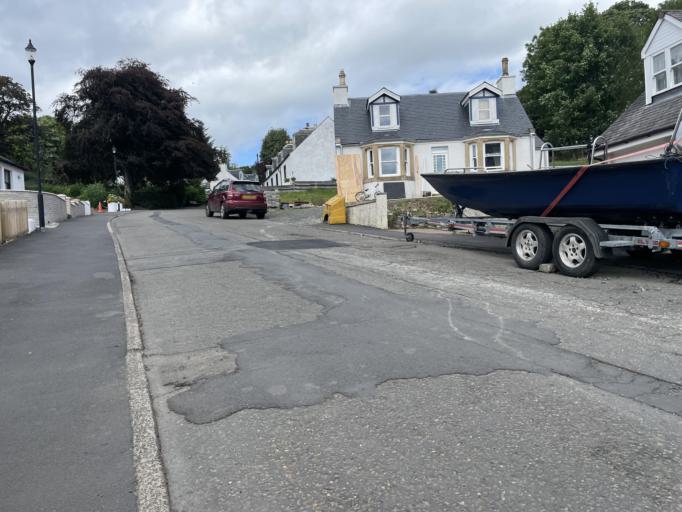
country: GB
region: Scotland
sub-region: South Ayrshire
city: Maybole
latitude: 55.2111
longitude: -4.7104
